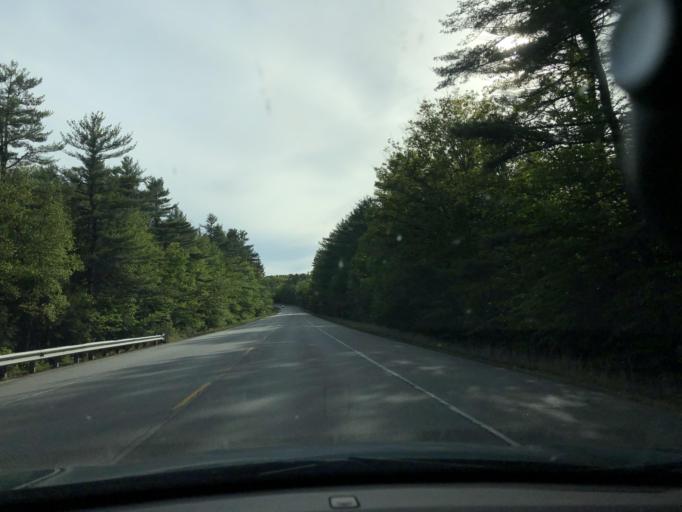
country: US
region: New Hampshire
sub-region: Merrimack County
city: New London
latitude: 43.4155
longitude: -71.9413
